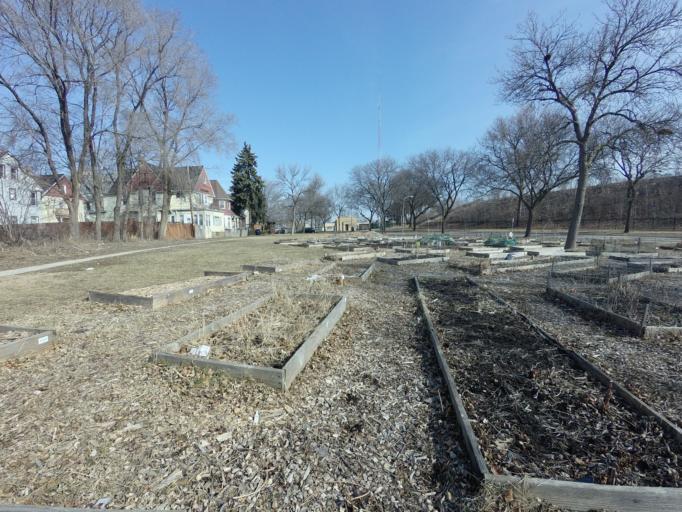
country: US
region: Wisconsin
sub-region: Milwaukee County
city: Milwaukee
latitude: 43.0594
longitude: -87.9032
